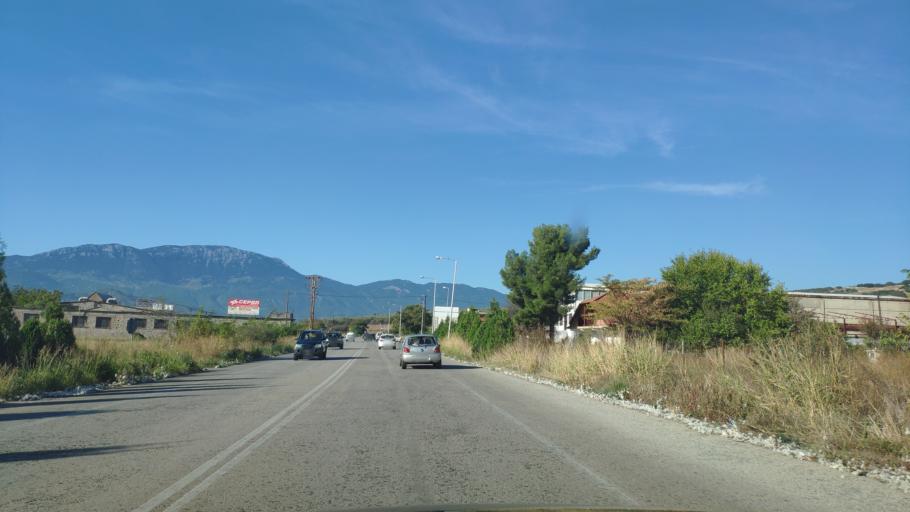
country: GR
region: Central Greece
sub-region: Nomos Voiotias
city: Livadeia
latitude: 38.4617
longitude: 22.9061
